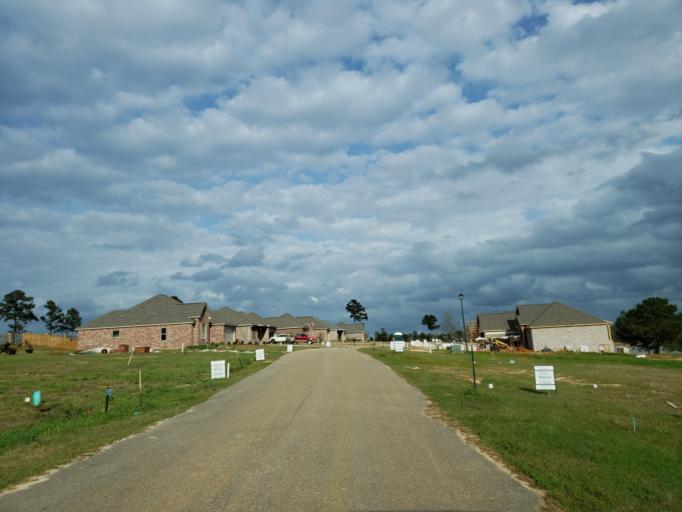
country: US
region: Mississippi
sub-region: Jones County
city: Ellisville
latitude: 31.5575
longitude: -89.2568
